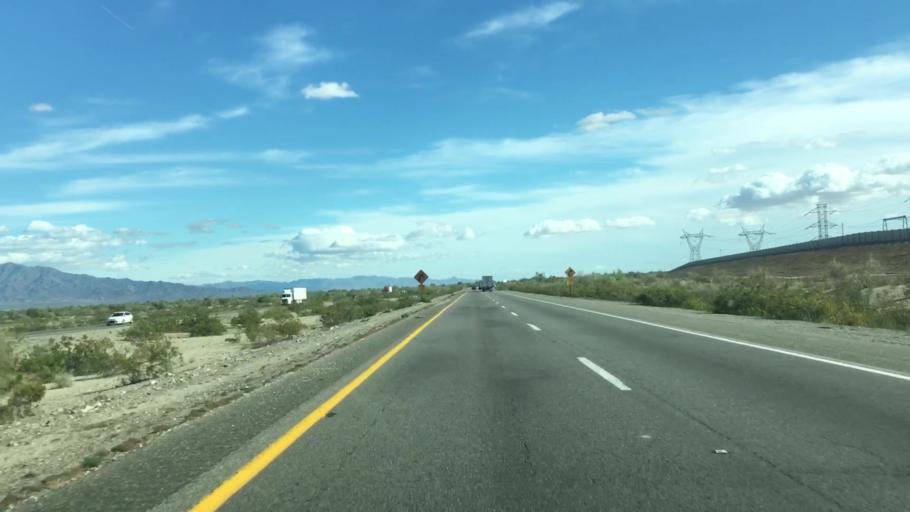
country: US
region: California
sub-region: Imperial County
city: Niland
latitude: 33.7022
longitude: -115.3149
